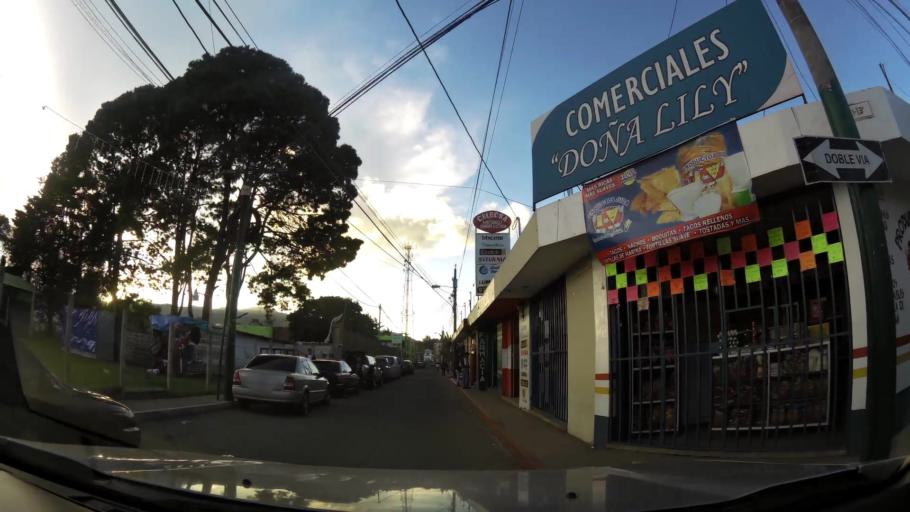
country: GT
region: Sacatepequez
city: San Lucas Sacatepequez
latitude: 14.6104
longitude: -90.6589
